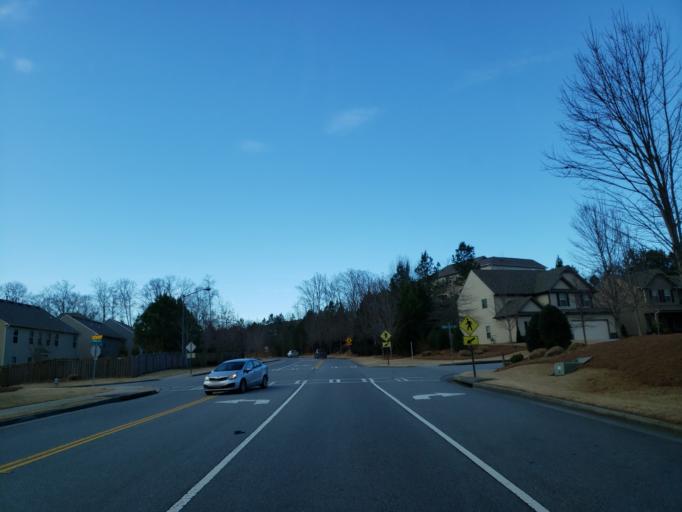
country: US
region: Georgia
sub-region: Cobb County
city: Kennesaw
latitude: 34.0597
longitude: -84.6080
